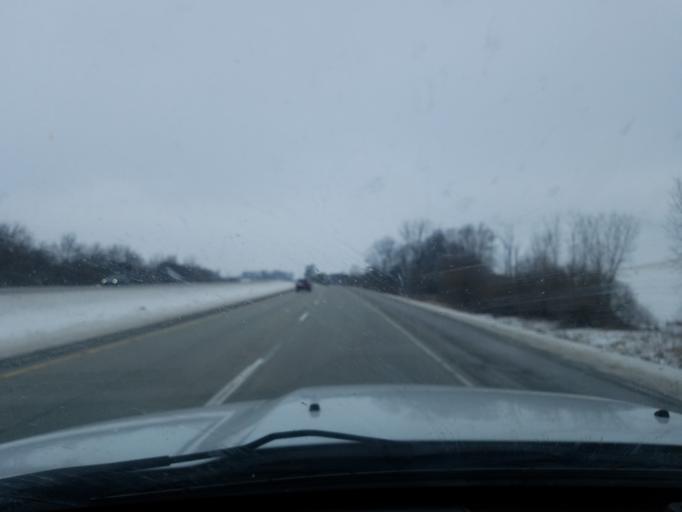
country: US
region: Indiana
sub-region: Marshall County
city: Argos
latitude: 41.1669
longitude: -86.2398
